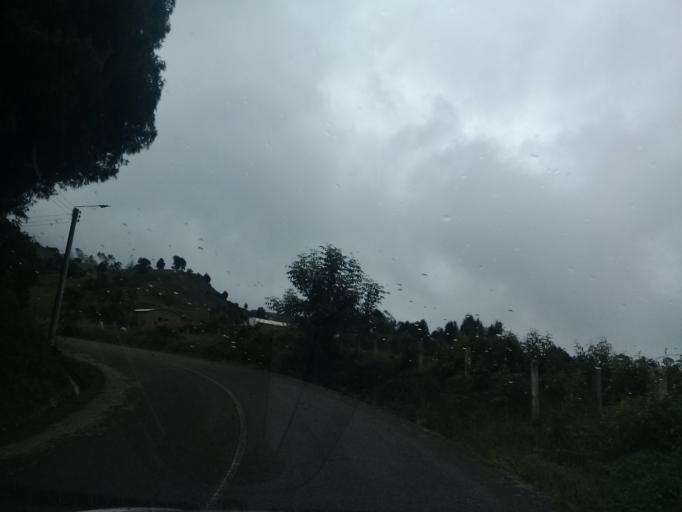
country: CO
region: Boyaca
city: Samaca
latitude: 5.4509
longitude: -73.4275
